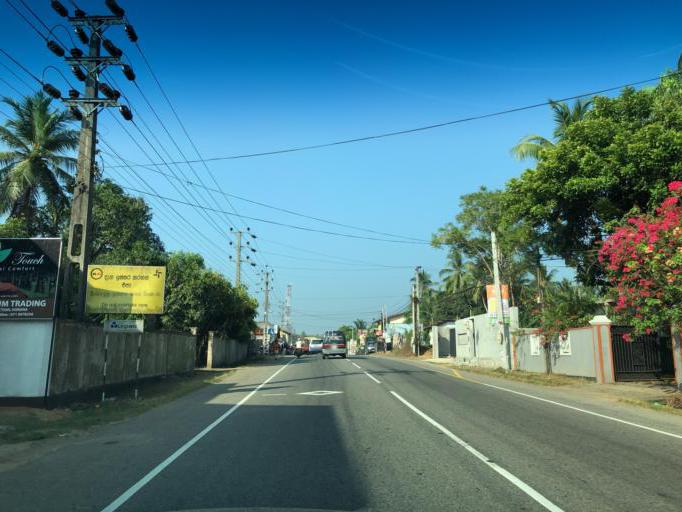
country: LK
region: Western
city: Horana South
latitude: 6.7242
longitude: 80.0913
